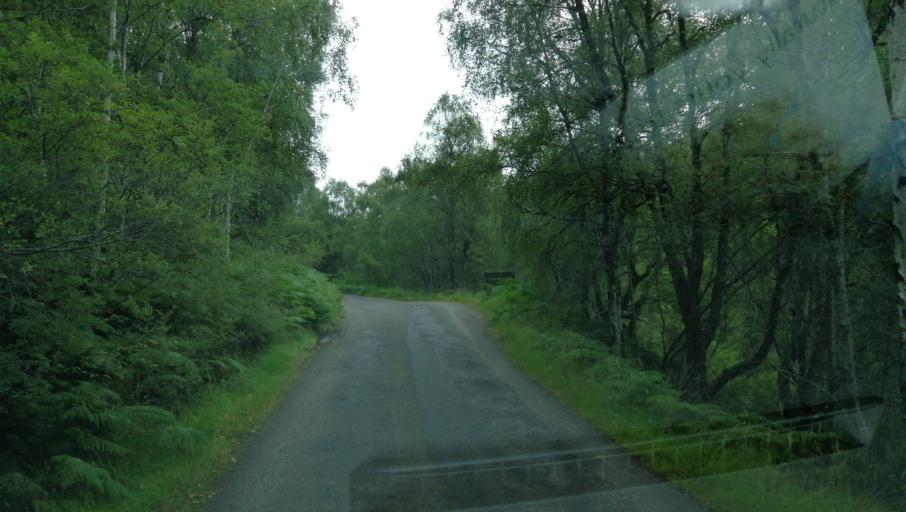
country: GB
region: Scotland
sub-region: Highland
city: Beauly
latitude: 57.3129
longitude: -4.8510
